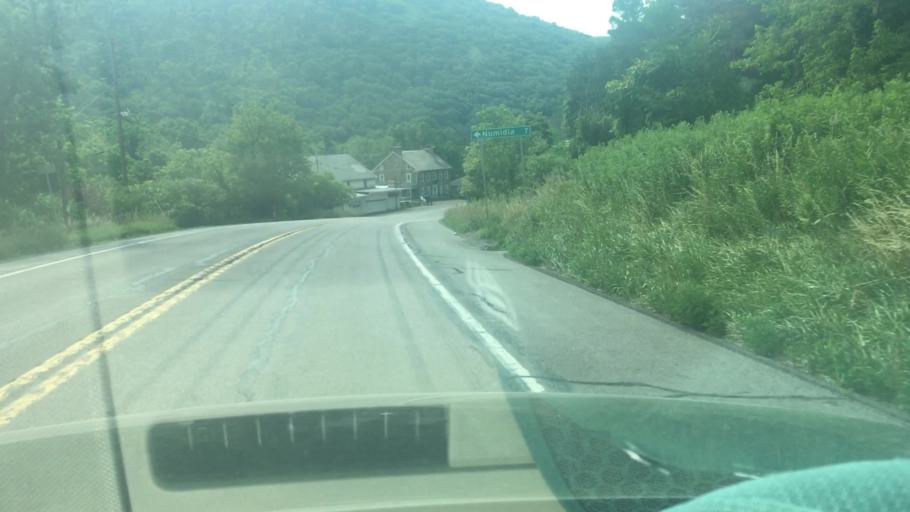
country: US
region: Pennsylvania
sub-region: Northumberland County
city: Kulpmont
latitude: 40.8330
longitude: -76.5068
